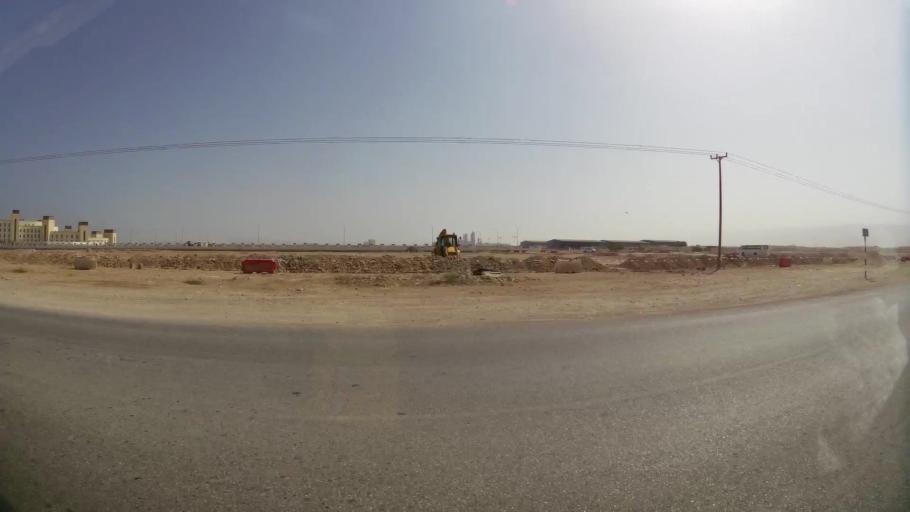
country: OM
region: Zufar
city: Salalah
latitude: 16.9885
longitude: 54.0145
